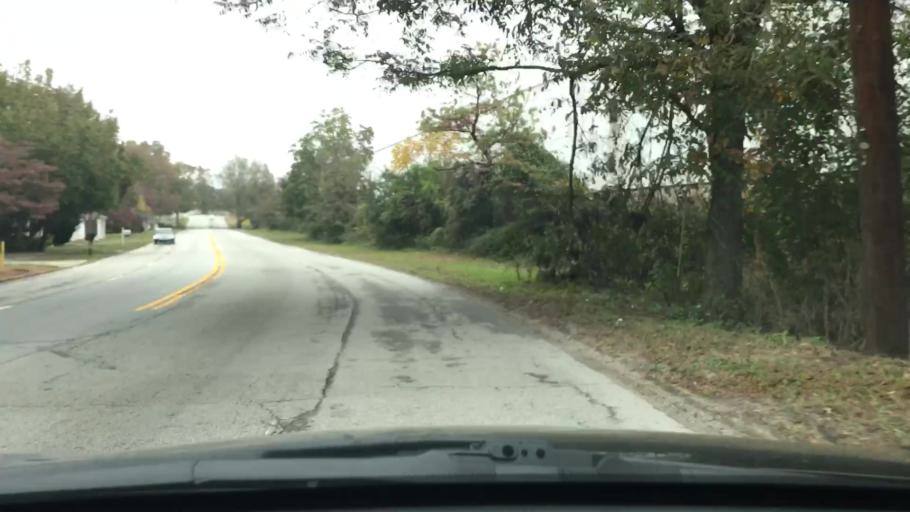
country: US
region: Georgia
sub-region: DeKalb County
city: Scottdale
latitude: 33.7868
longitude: -84.2647
